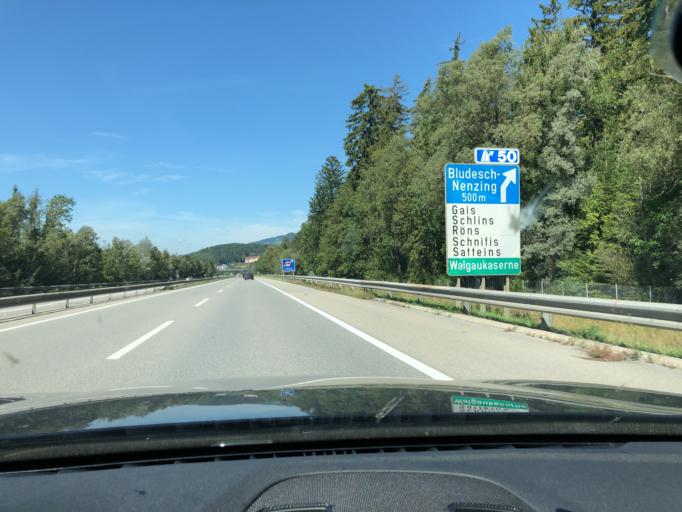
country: AT
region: Vorarlberg
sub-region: Politischer Bezirk Bludenz
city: Bludesch
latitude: 47.1855
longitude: 9.7233
